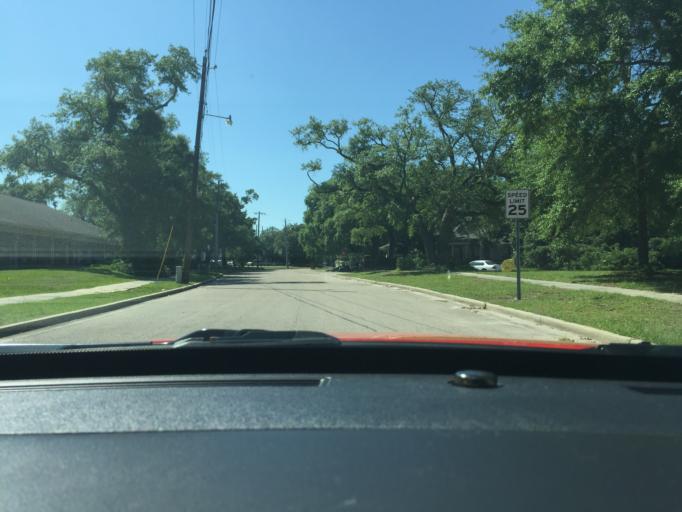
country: US
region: Mississippi
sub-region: Harrison County
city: Biloxi
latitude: 30.3912
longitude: -88.9863
